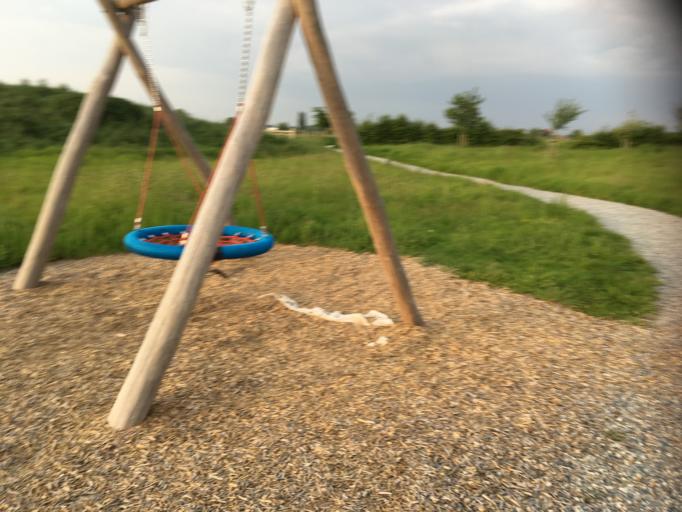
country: BE
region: Flanders
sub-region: Provincie West-Vlaanderen
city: Ardooie
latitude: 50.9811
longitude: 3.2053
